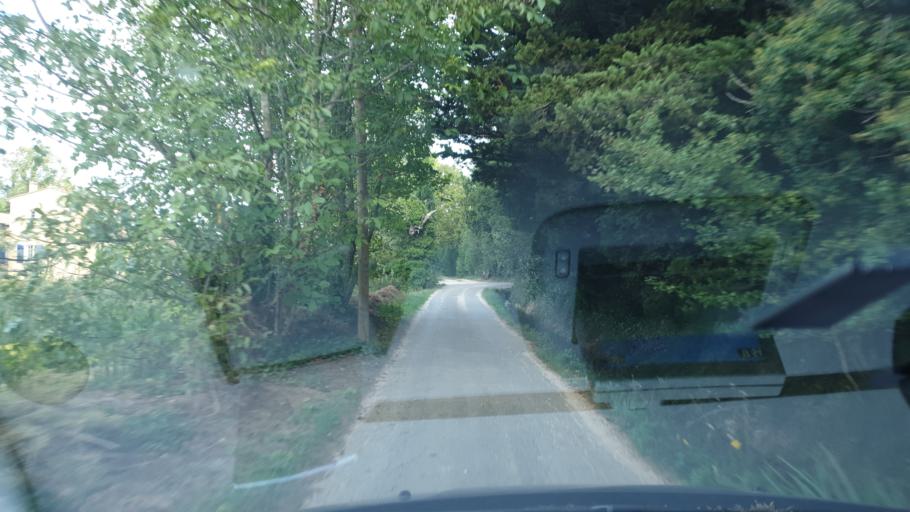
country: FR
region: Provence-Alpes-Cote d'Azur
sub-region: Departement du Vaucluse
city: Monteux
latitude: 44.0481
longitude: 5.0065
